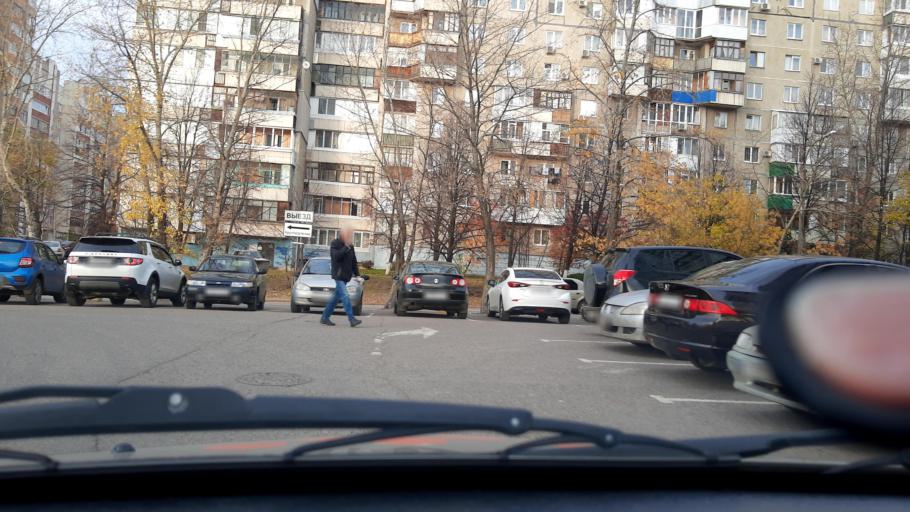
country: RU
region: Bashkortostan
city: Ufa
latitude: 54.7176
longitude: 56.0081
